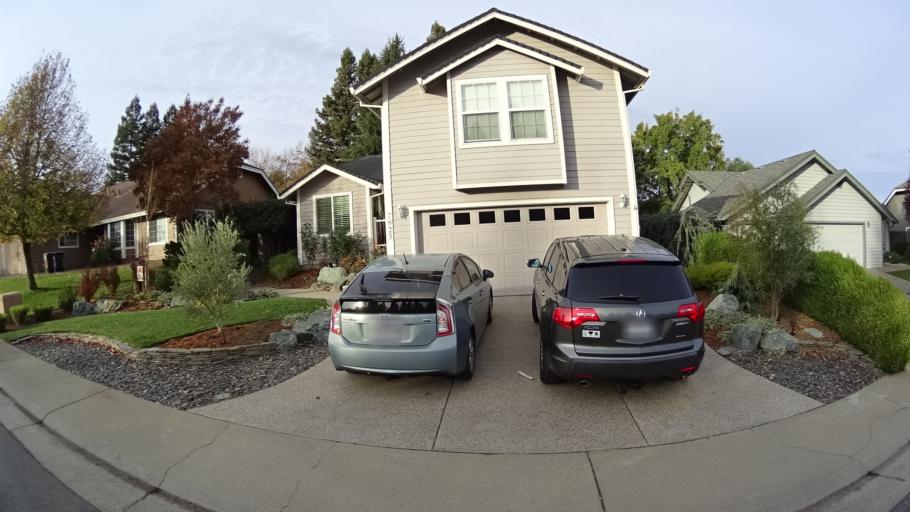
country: US
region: California
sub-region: Sacramento County
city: Citrus Heights
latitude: 38.7090
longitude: -121.2746
